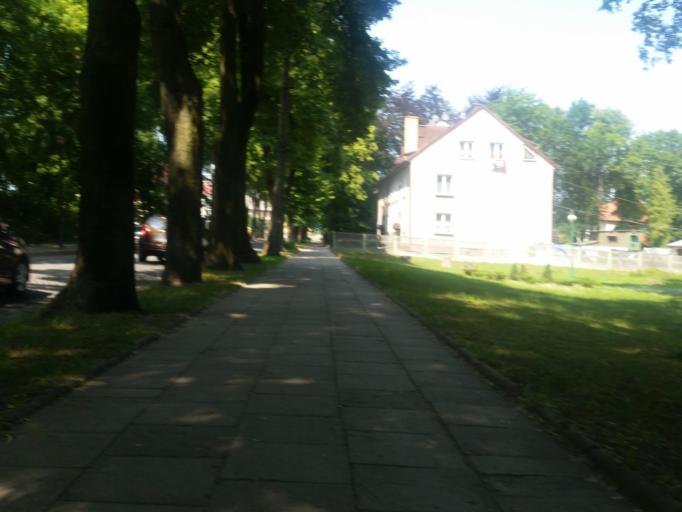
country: PL
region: Warmian-Masurian Voivodeship
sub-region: Powiat goldapski
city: Goldap
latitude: 54.3121
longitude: 22.3065
